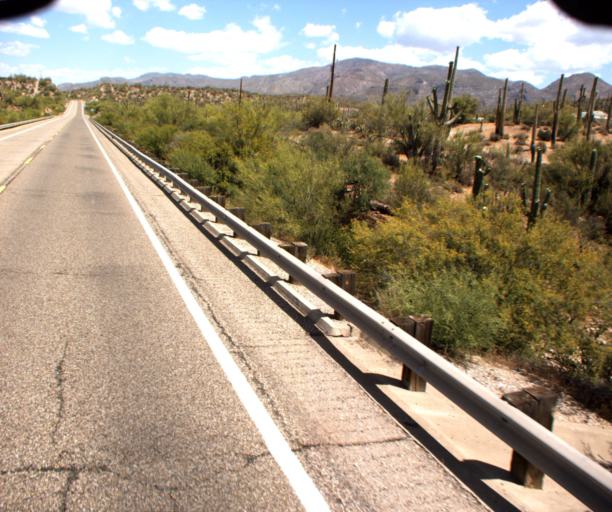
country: US
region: Arizona
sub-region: Pinal County
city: Kearny
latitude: 33.0911
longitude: -110.9298
